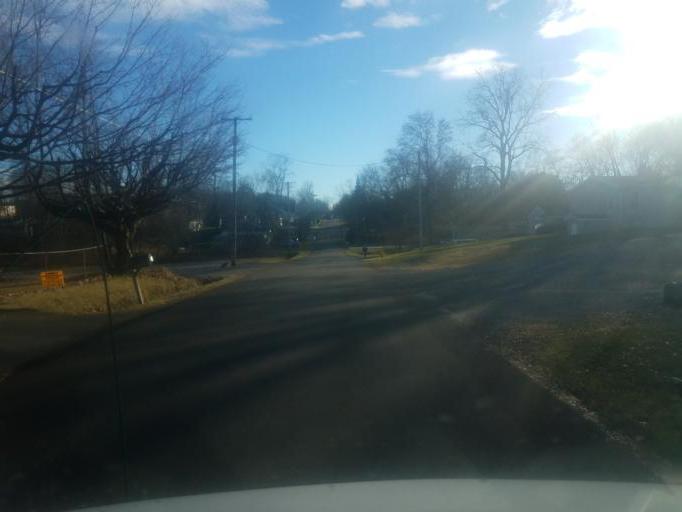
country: US
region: Ohio
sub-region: Richland County
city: Mansfield
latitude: 40.7901
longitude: -82.5485
